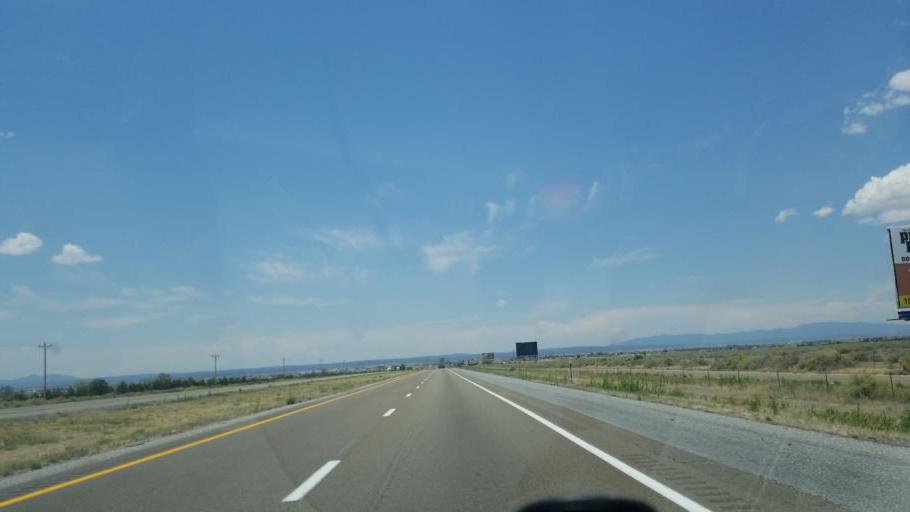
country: US
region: New Mexico
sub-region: Torrance County
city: Moriarty
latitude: 35.0049
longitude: -105.9822
